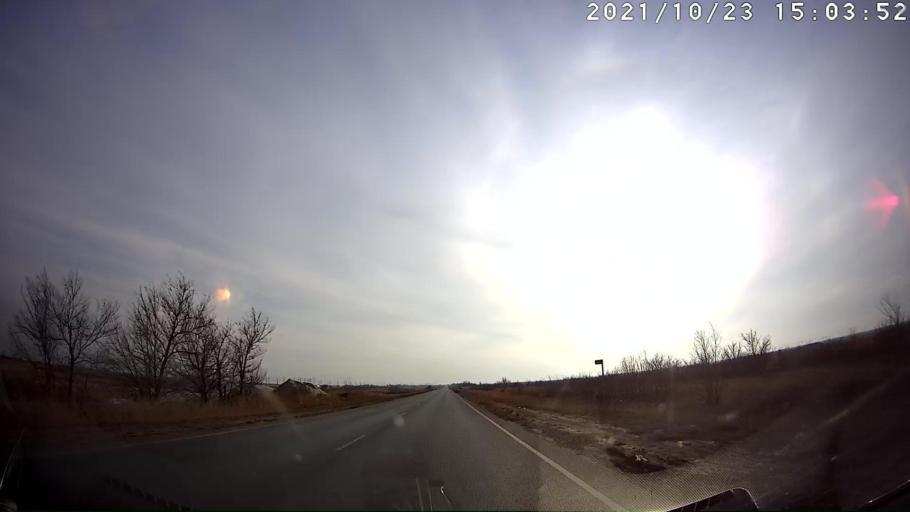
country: RU
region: Volgograd
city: Volgograd
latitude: 48.4068
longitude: 44.3728
